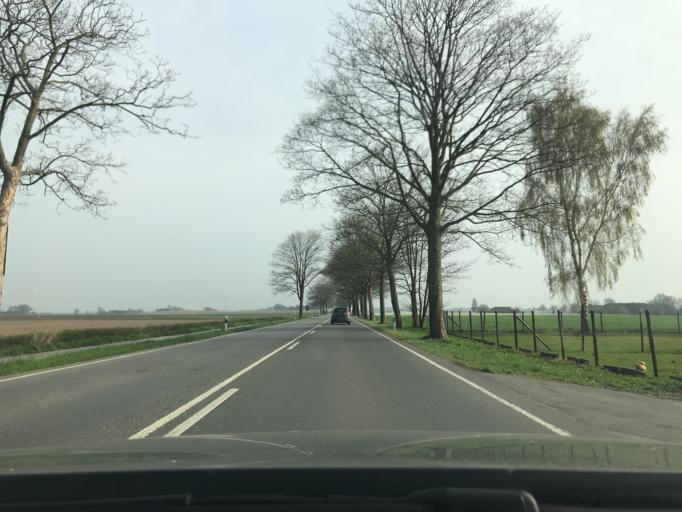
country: DE
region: North Rhine-Westphalia
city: Geldern
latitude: 51.4881
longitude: 6.3361
